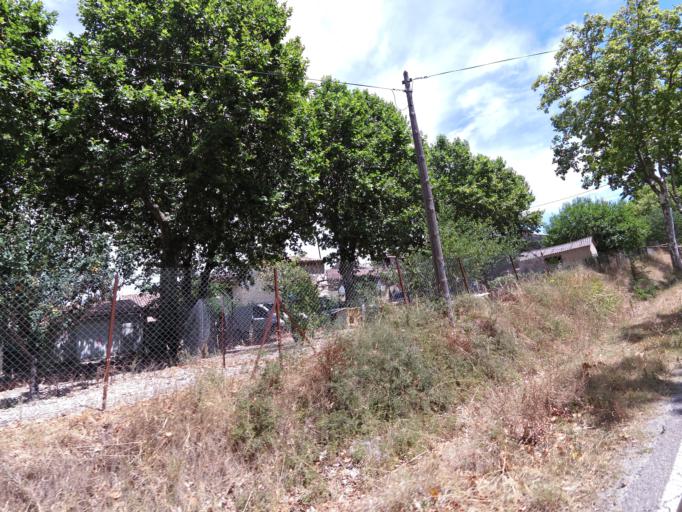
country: FR
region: Languedoc-Roussillon
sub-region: Departement du Gard
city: Saint-Hippolyte-du-Fort
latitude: 43.9563
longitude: 3.8679
